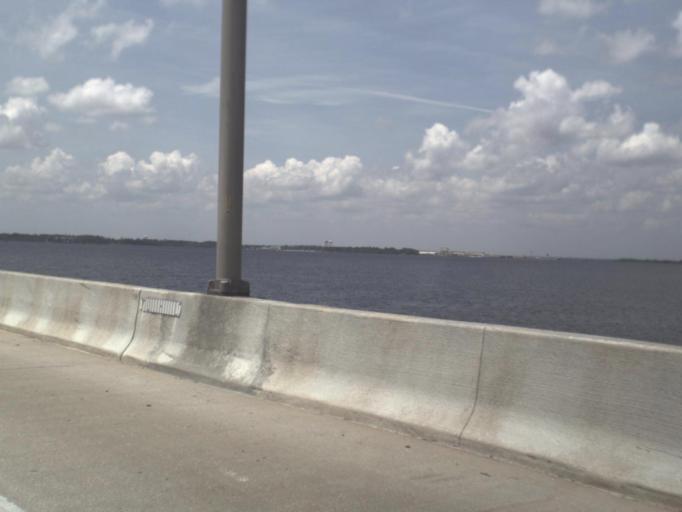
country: US
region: Florida
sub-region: Clay County
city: Orange Park
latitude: 30.1886
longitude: -81.6461
